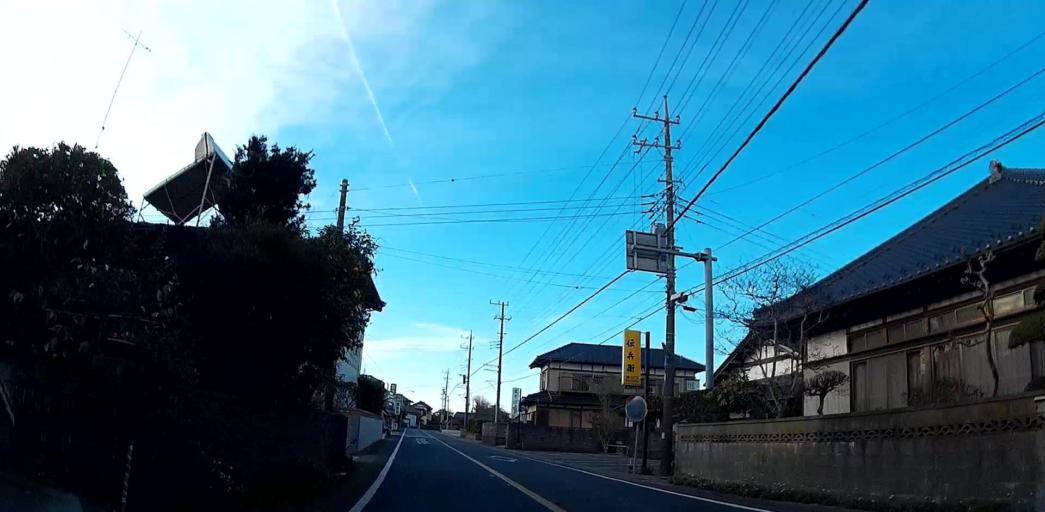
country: JP
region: Chiba
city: Omigawa
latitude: 35.8323
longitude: 140.6914
